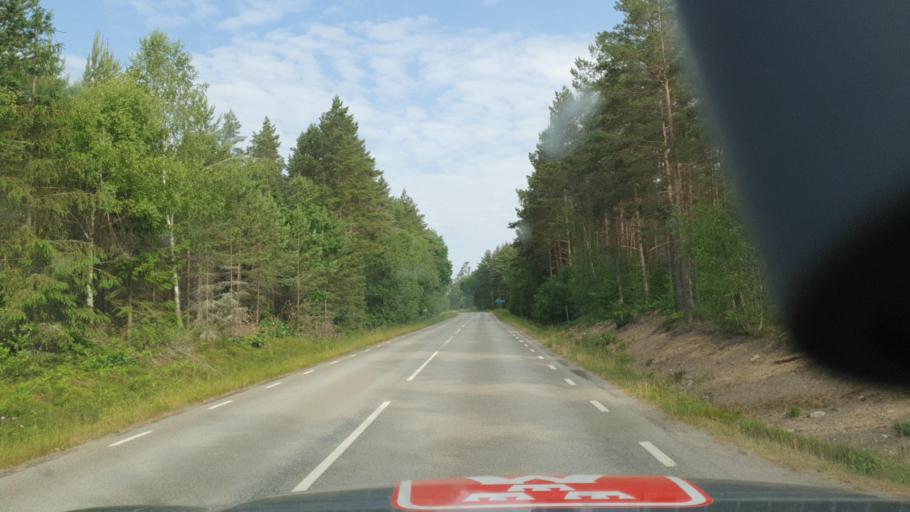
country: SE
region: Kalmar
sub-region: Nybro Kommun
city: Nybro
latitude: 56.6700
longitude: 15.9927
